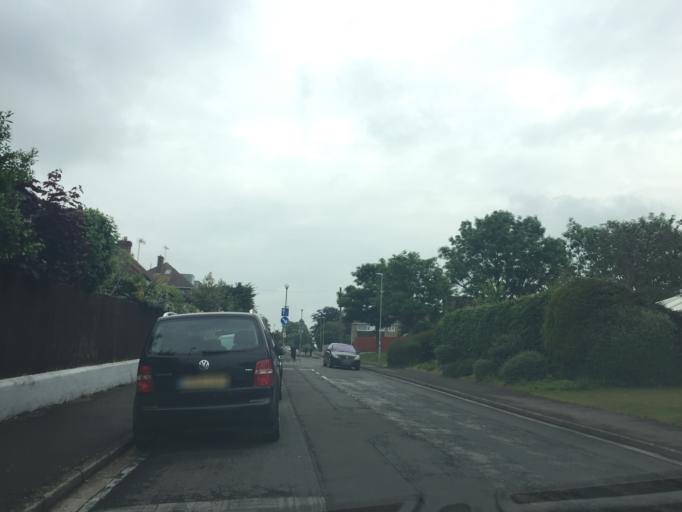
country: GB
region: England
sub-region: Dorset
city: Dorchester
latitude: 50.7050
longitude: -2.4500
